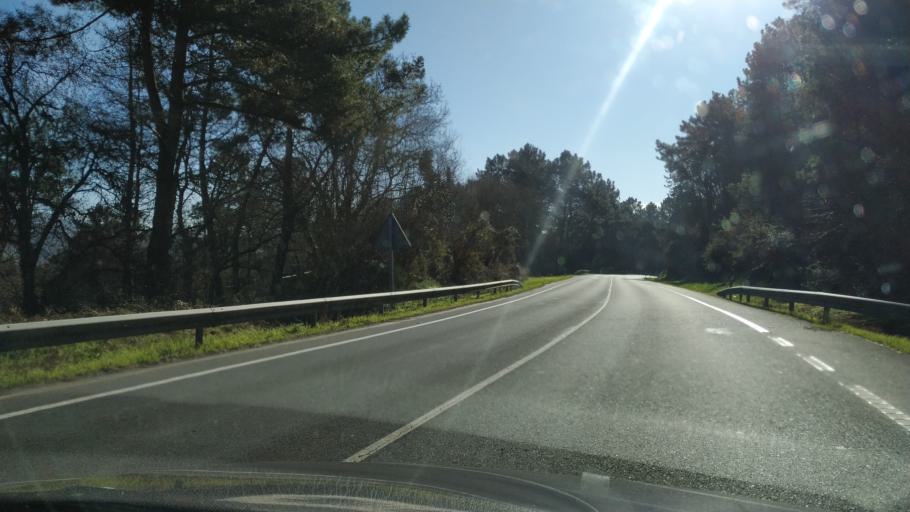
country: ES
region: Galicia
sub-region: Provincia da Coruna
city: Ribeira
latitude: 42.7467
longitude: -8.3403
